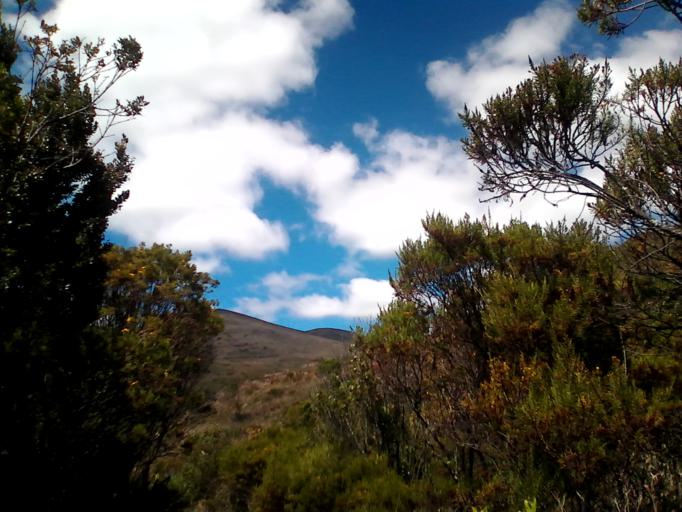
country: CO
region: Boyaca
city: Santa Rosa de Viterbo
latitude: 5.9105
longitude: -73.0518
